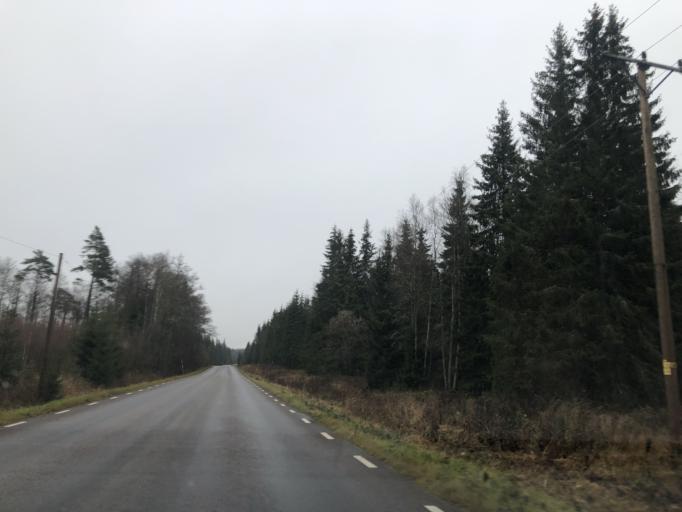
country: SE
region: Vaestra Goetaland
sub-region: Ulricehamns Kommun
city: Ulricehamn
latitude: 57.7501
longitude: 13.5211
